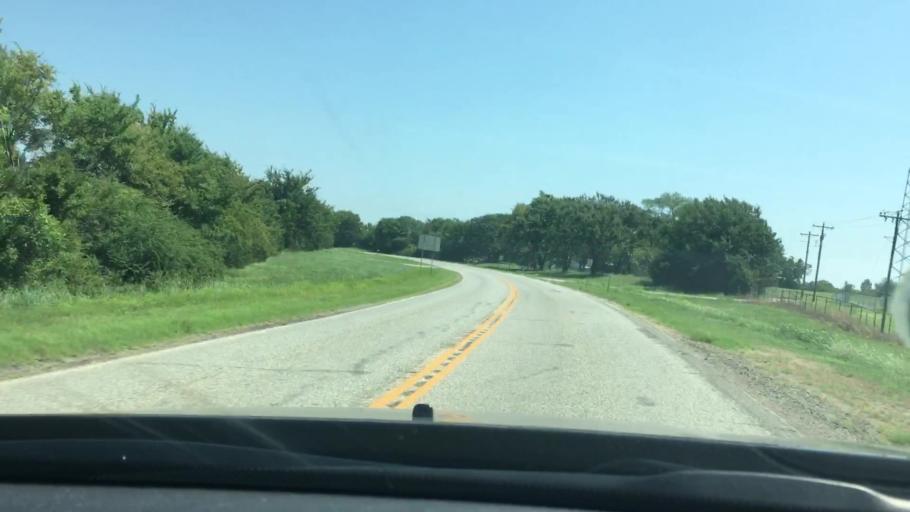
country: US
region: Oklahoma
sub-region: Johnston County
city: Tishomingo
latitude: 34.2377
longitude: -96.5609
